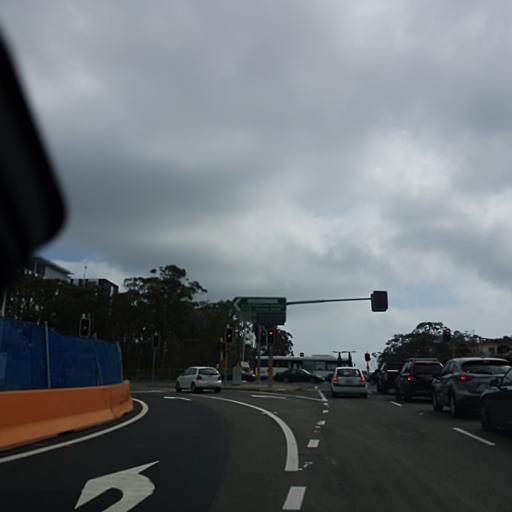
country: AU
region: New South Wales
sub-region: Warringah
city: Allambie Heights
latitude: -33.7528
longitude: 151.2342
